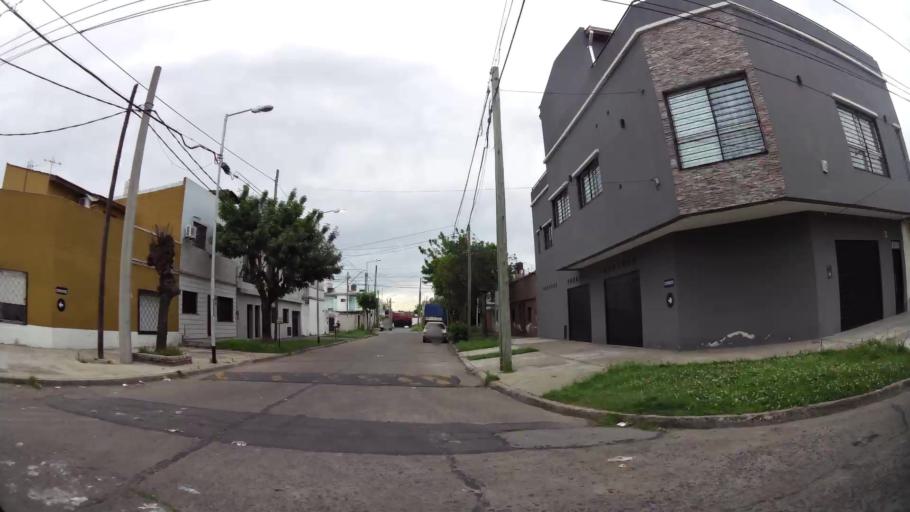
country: AR
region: Buenos Aires
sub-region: Partido de Avellaneda
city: Avellaneda
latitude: -34.6863
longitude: -58.3690
